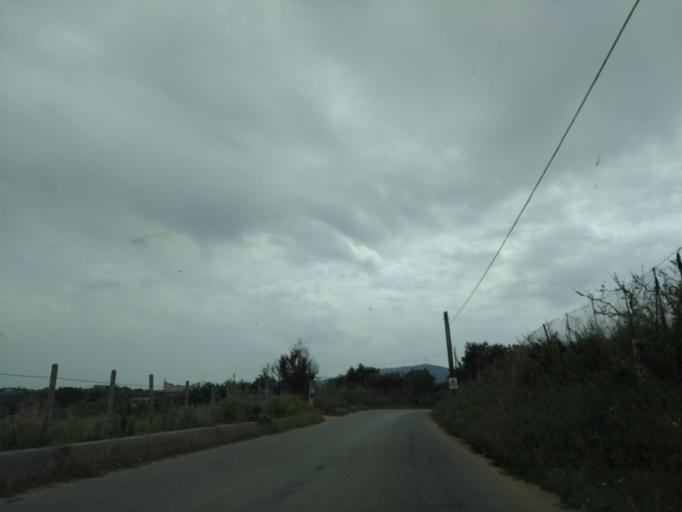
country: IT
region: Sicily
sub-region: Palermo
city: Partinico
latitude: 38.0051
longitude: 13.0680
